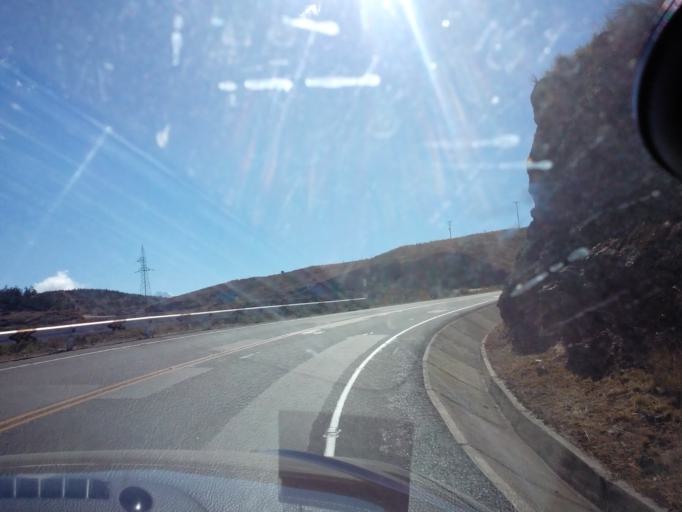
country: PE
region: Apurimac
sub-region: Provincia de Abancay
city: Tamburco
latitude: -13.5852
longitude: -72.8192
